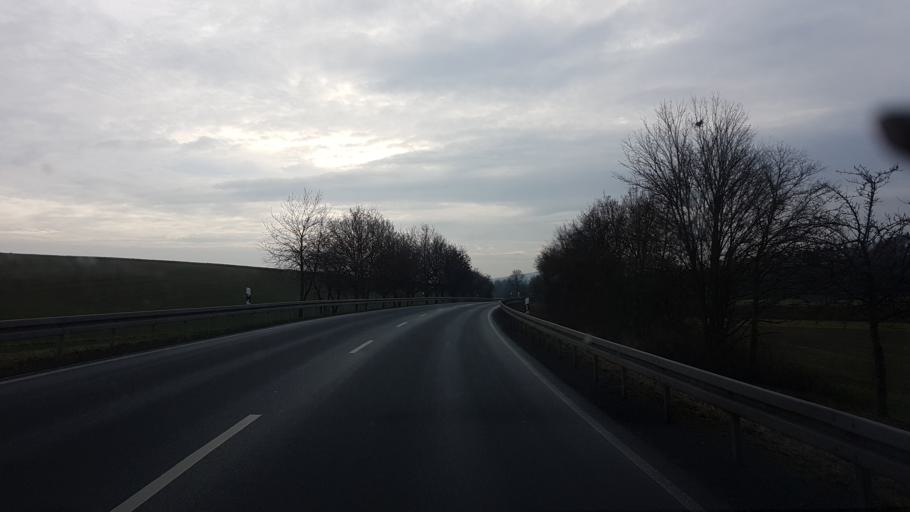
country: DE
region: Bavaria
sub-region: Regierungsbezirk Unterfranken
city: Pfarrweisach
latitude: 50.1569
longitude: 10.7350
